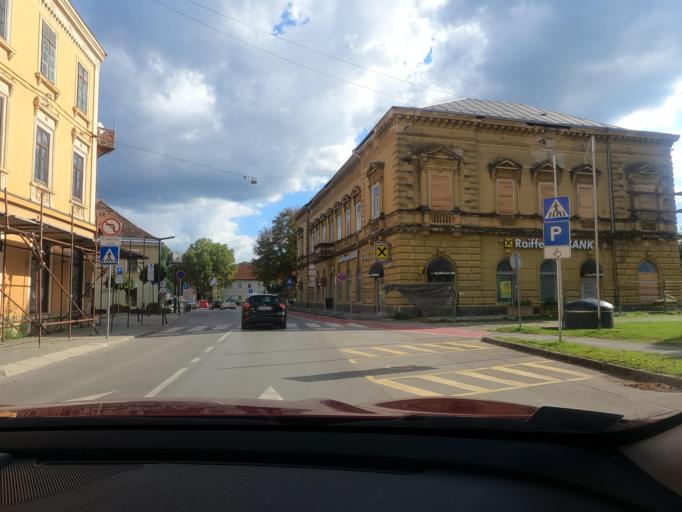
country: HR
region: Sisacko-Moslavacka
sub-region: Grad Sisak
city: Sisak
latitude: 45.4856
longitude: 16.3708
